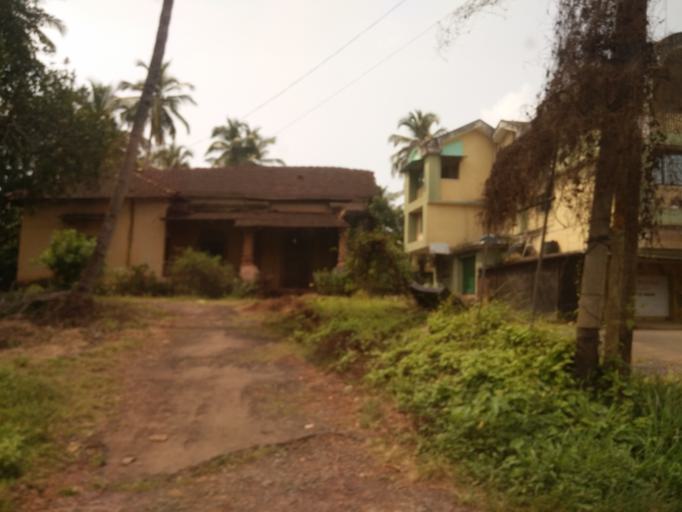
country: IN
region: Goa
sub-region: South Goa
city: Madgaon
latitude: 15.2472
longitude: 73.9711
